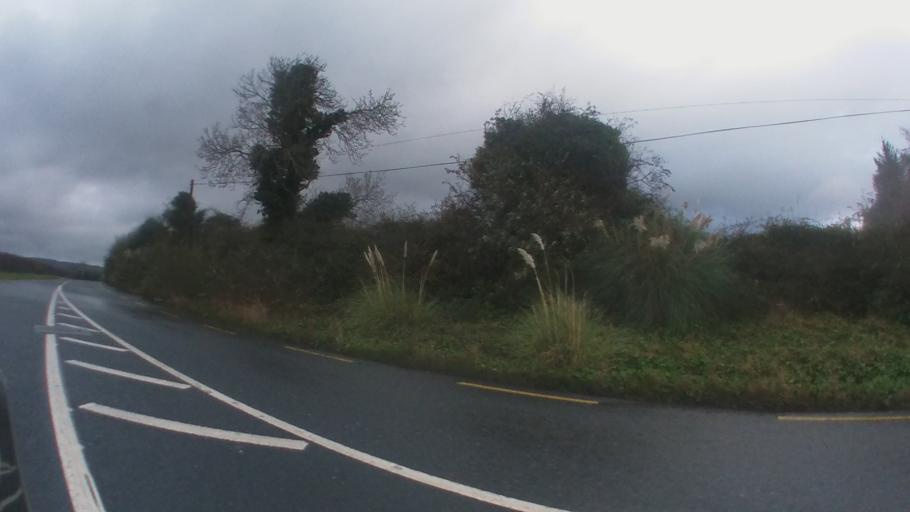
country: IE
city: Kilquade
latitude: 53.0969
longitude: -6.0854
